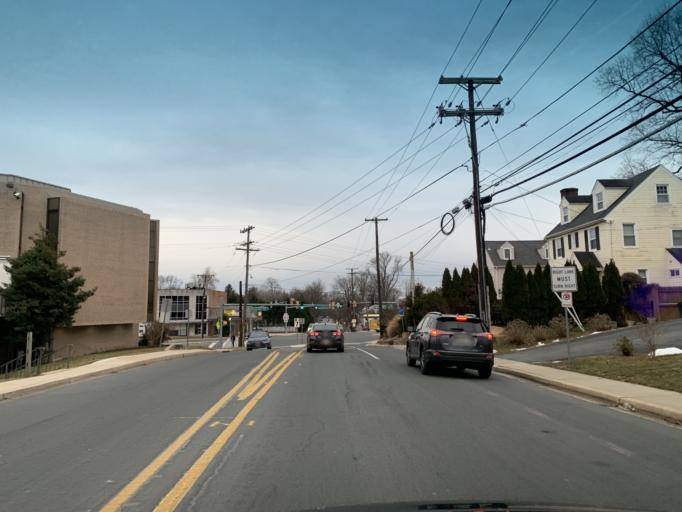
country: US
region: Maryland
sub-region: Montgomery County
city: North Kensington
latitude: 39.0346
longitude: -77.0726
